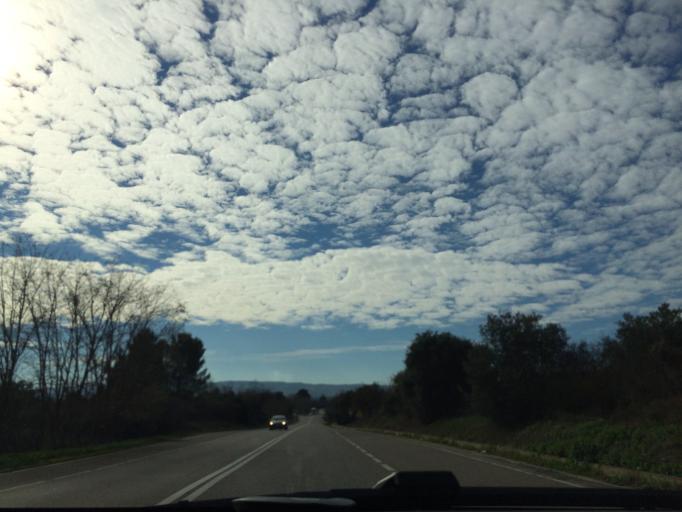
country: IT
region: Basilicate
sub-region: Provincia di Matera
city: Matera
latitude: 40.6138
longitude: 16.5766
